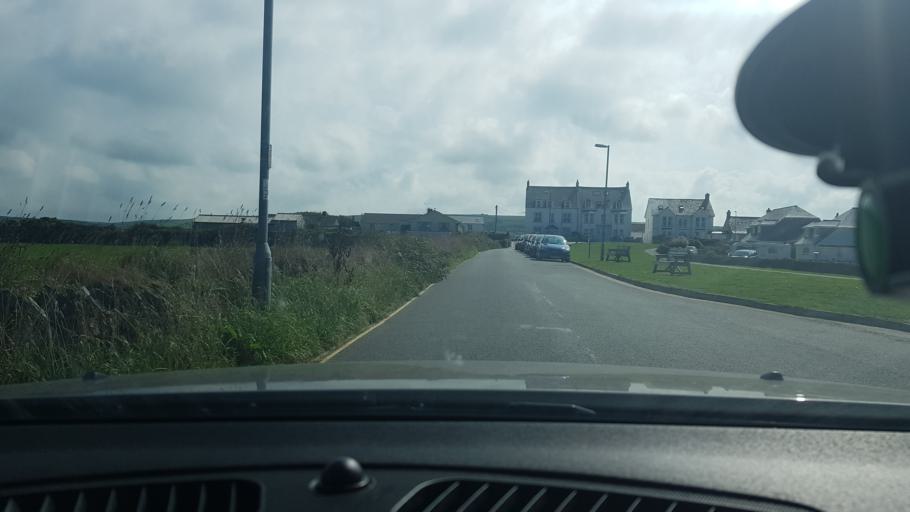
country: GB
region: England
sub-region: Cornwall
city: Tintagel
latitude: 50.6672
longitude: -4.7533
